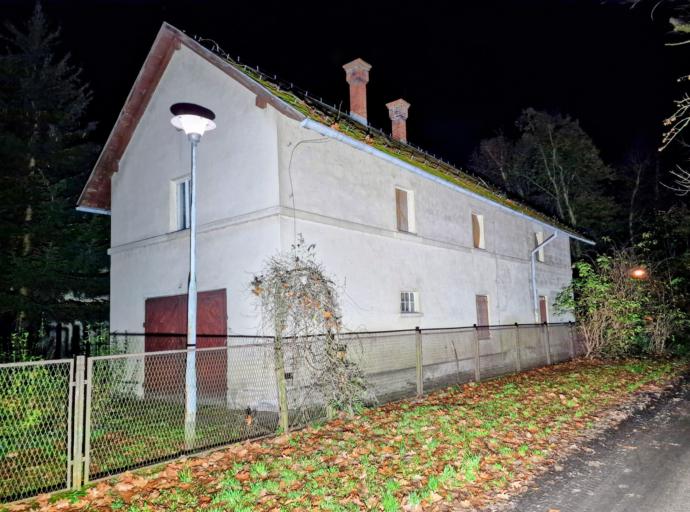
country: PL
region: Lubusz
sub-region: Powiat zielonogorski
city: Klenica
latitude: 51.9895
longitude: 15.7796
